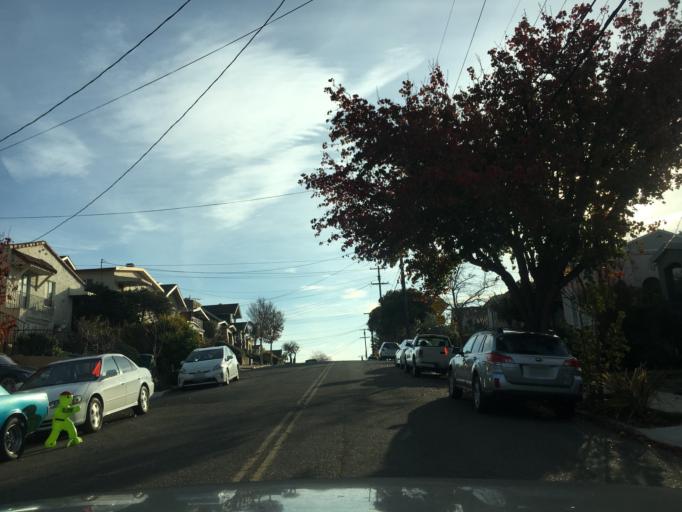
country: US
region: California
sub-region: Alameda County
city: Albany
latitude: 37.8864
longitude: -122.2847
